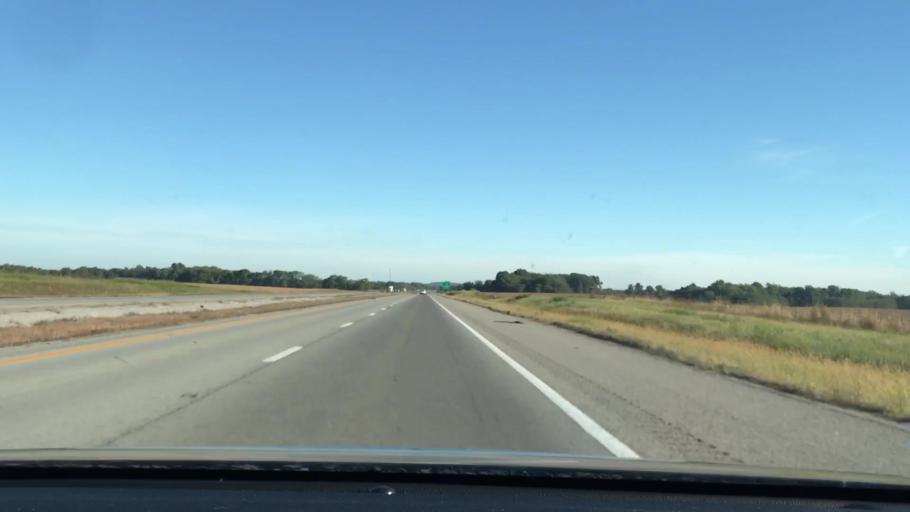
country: US
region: Kentucky
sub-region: Christian County
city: Hopkinsville
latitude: 36.7857
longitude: -87.4963
